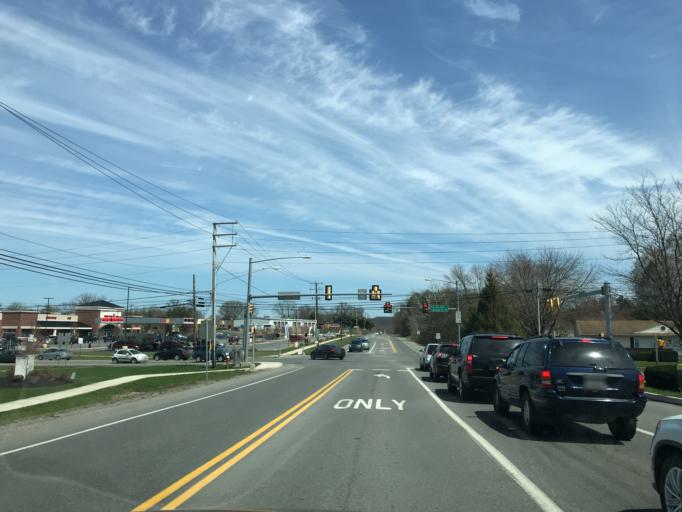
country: US
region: Pennsylvania
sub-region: Snyder County
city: Selinsgrove
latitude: 40.8096
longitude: -76.8673
